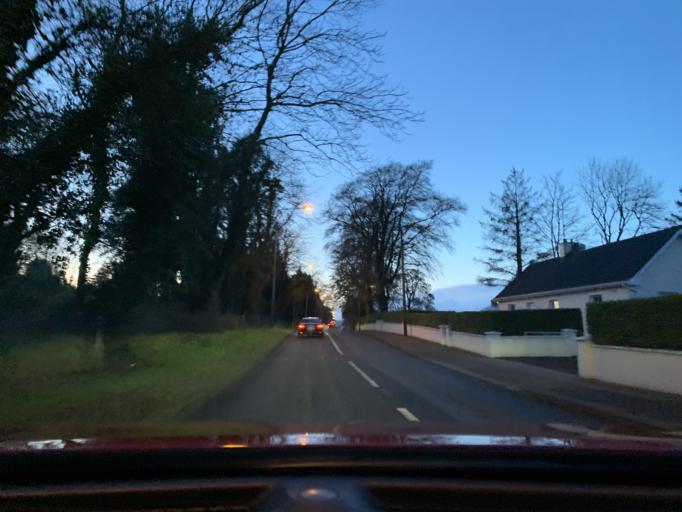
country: IE
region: Connaught
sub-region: Roscommon
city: Boyle
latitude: 53.9693
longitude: -8.2765
